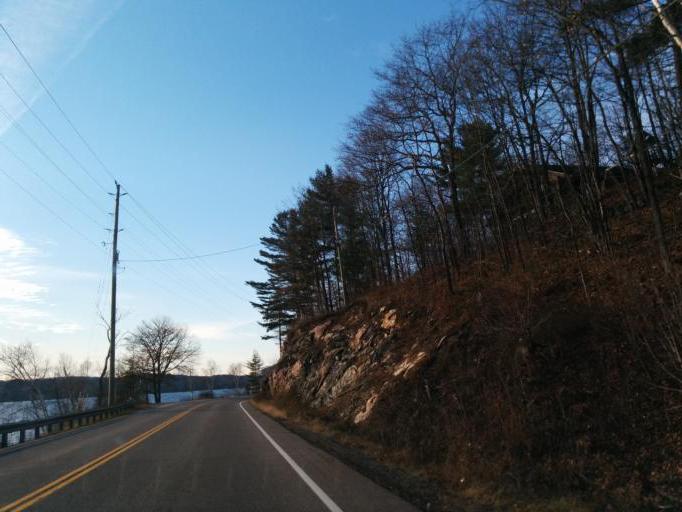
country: CA
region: Ontario
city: Bancroft
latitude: 45.0220
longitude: -78.3637
